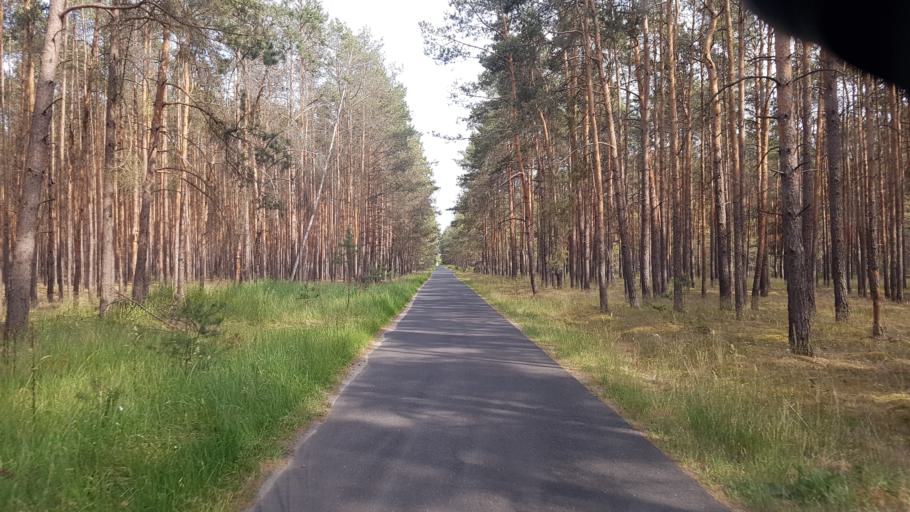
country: DE
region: Brandenburg
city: Herzberg
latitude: 51.7661
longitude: 13.2417
